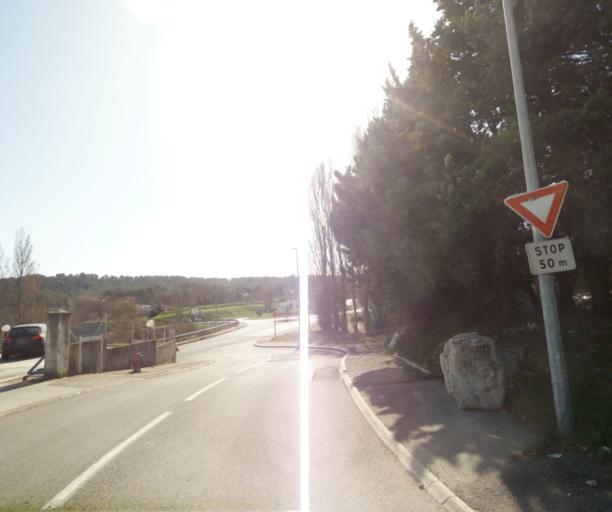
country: FR
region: Provence-Alpes-Cote d'Azur
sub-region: Departement des Bouches-du-Rhone
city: Cabries
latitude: 43.4267
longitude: 5.3925
